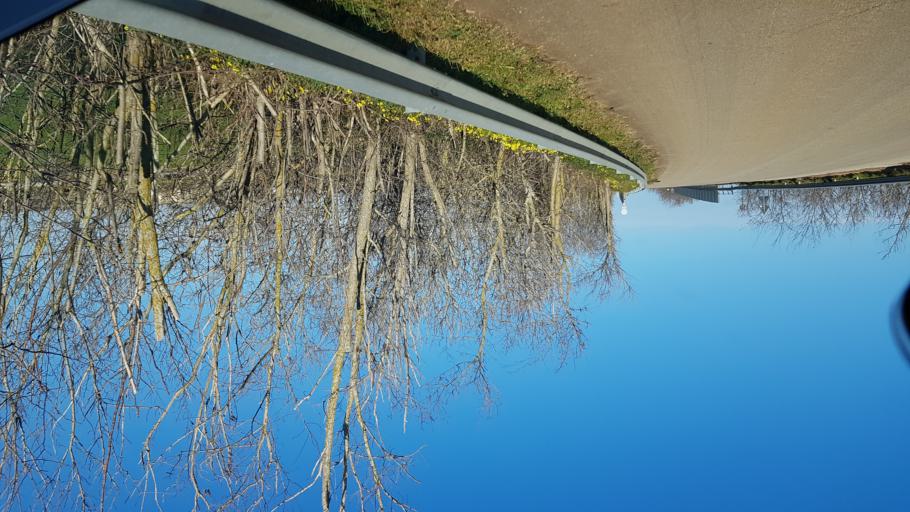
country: IT
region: Apulia
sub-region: Provincia di Brindisi
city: San Vito dei Normanni
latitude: 40.6887
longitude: 17.8232
